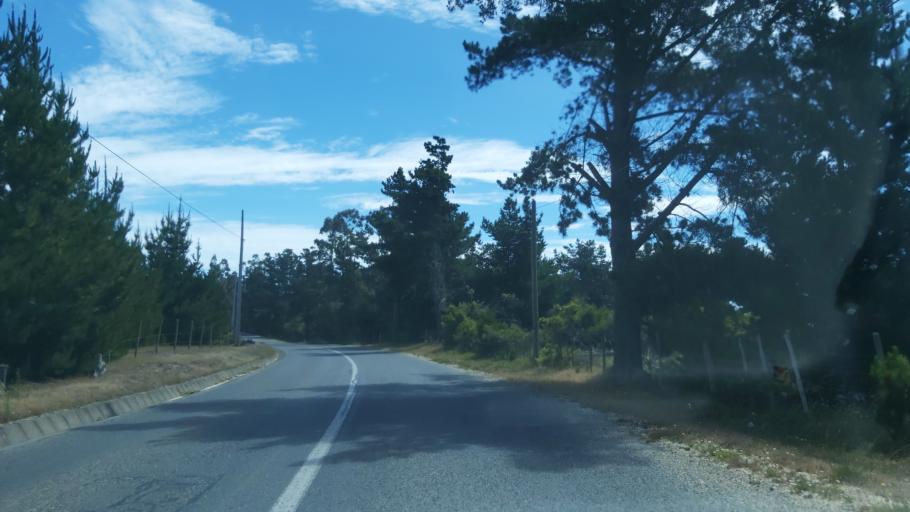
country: CL
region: Maule
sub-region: Provincia de Talca
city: Constitucion
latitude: -35.5526
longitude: -72.5790
